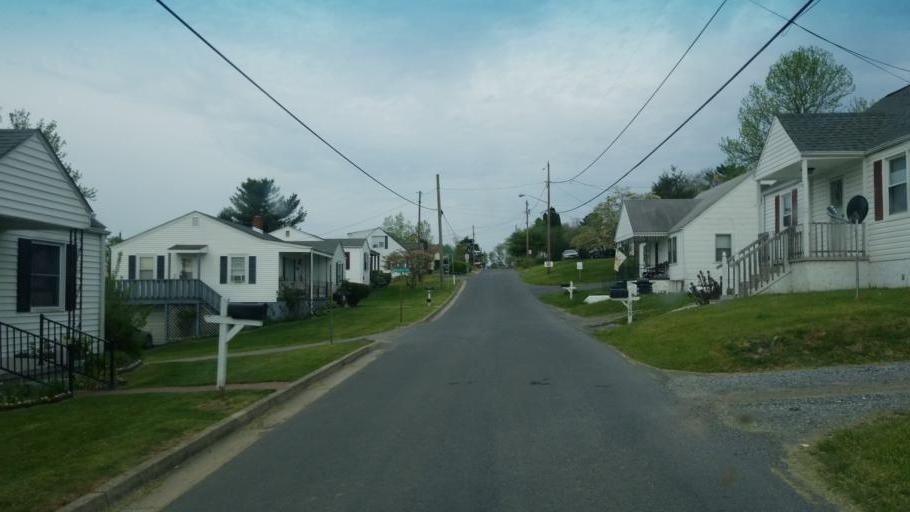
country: US
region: Virginia
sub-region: Smyth County
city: Marion
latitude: 36.8417
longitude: -81.5230
